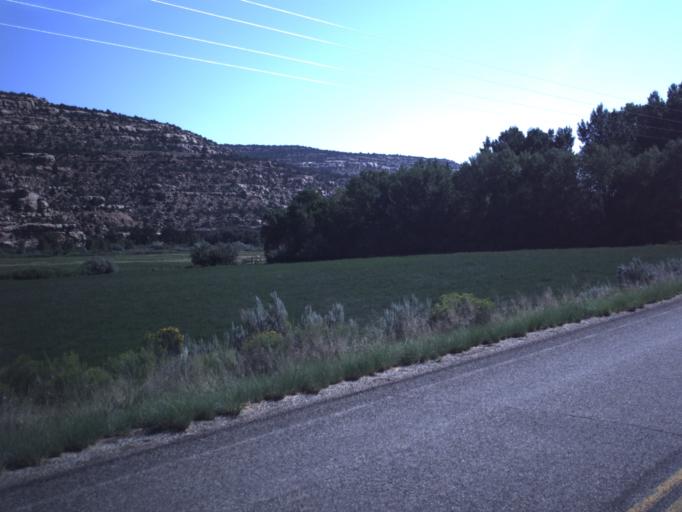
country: US
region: Utah
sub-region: Duchesne County
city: Duchesne
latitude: 40.2962
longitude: -110.5632
